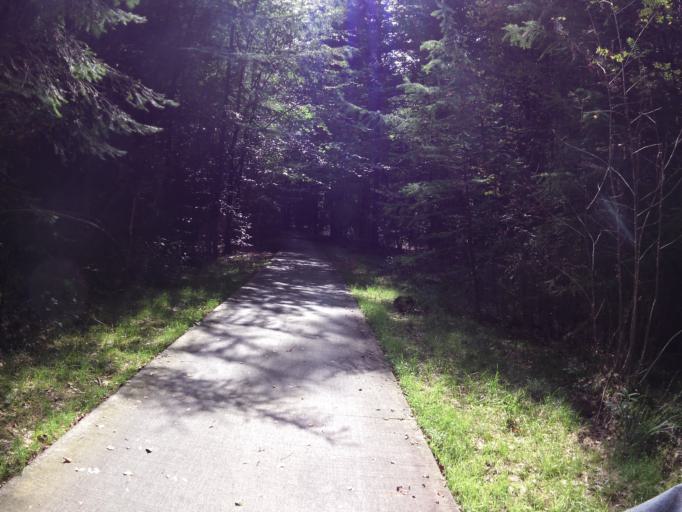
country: NL
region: Drenthe
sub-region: Gemeente Borger-Odoorn
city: Borger
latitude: 52.9475
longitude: 6.7510
